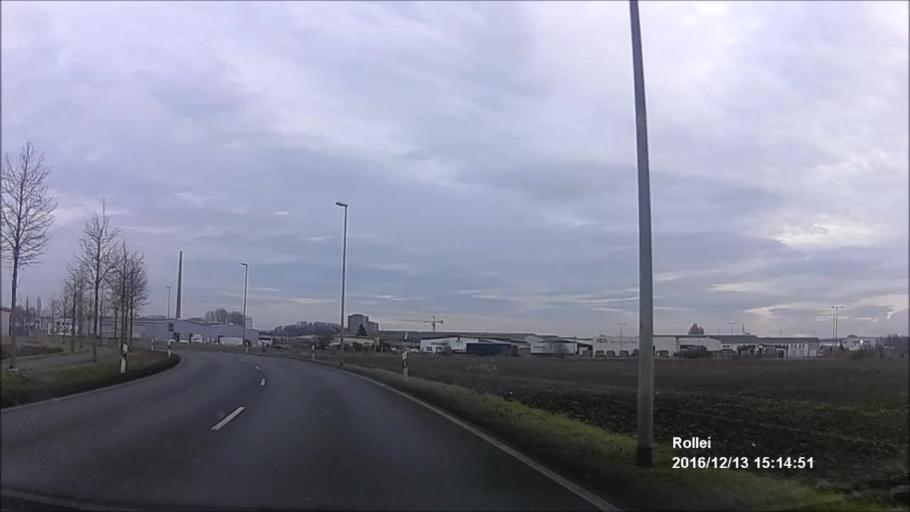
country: DE
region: Thuringia
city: Noda
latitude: 51.0266
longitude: 11.0039
